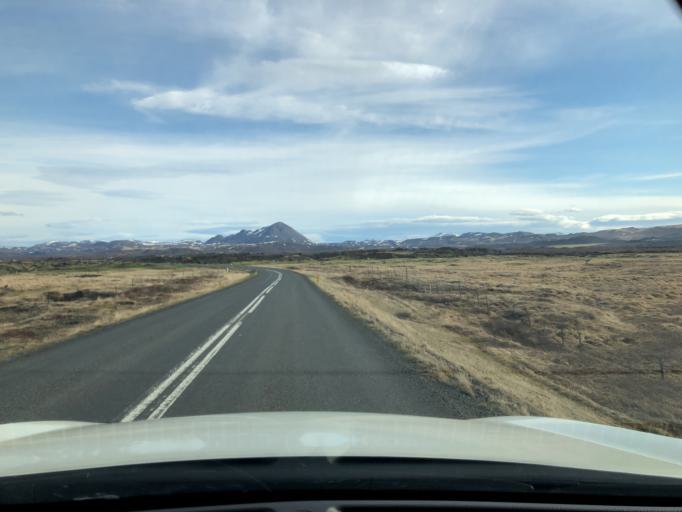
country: IS
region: Northeast
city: Laugar
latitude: 65.6110
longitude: -16.9171
